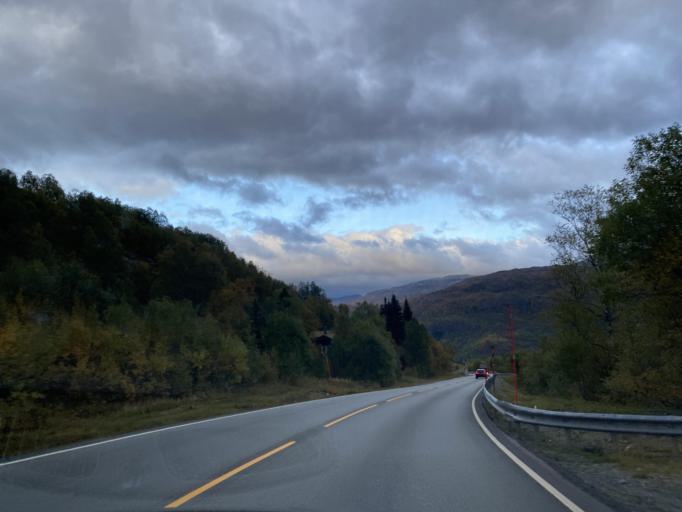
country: NO
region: Hordaland
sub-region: Odda
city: Odda
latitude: 59.8151
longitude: 6.7591
